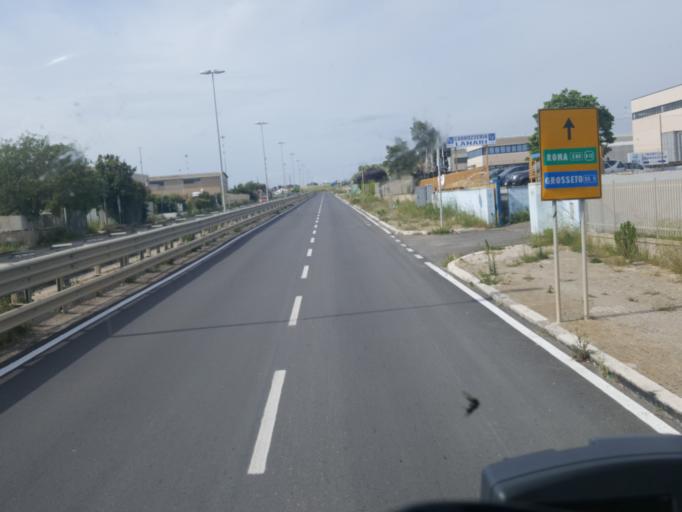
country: IT
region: Latium
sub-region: Citta metropolitana di Roma Capitale
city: Aurelia
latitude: 42.1210
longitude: 11.7784
